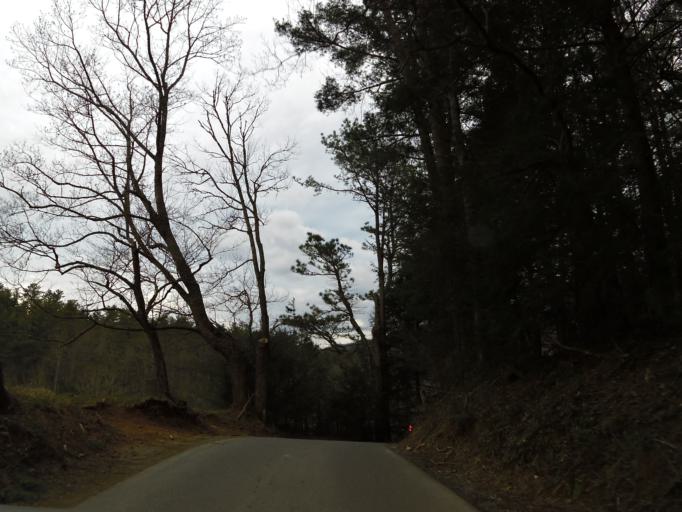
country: US
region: Tennessee
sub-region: Blount County
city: Wildwood
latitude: 35.5887
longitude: -83.8141
